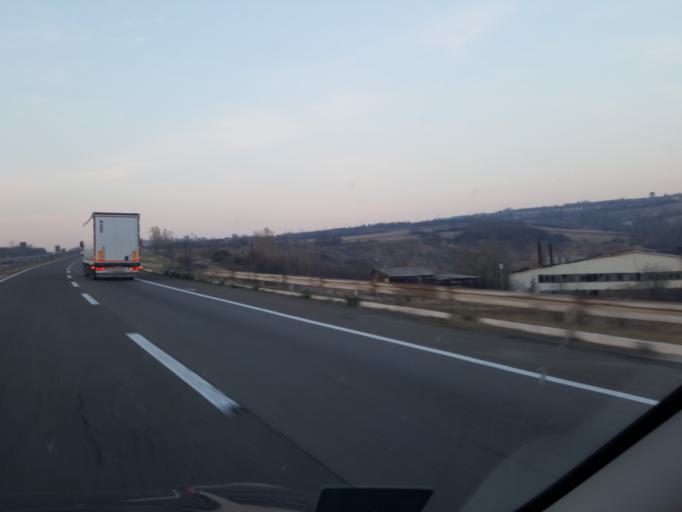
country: RS
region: Central Serbia
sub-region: Nisavski Okrug
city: Razanj
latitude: 43.6600
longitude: 21.5506
